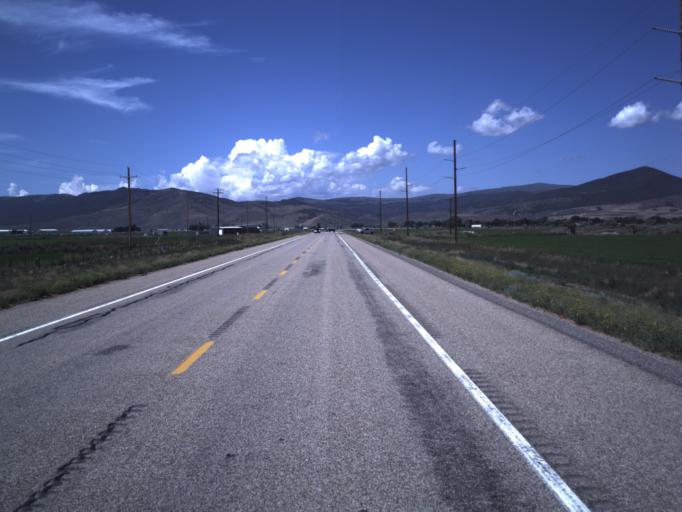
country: US
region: Utah
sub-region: Piute County
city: Junction
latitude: 38.1809
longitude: -112.2487
